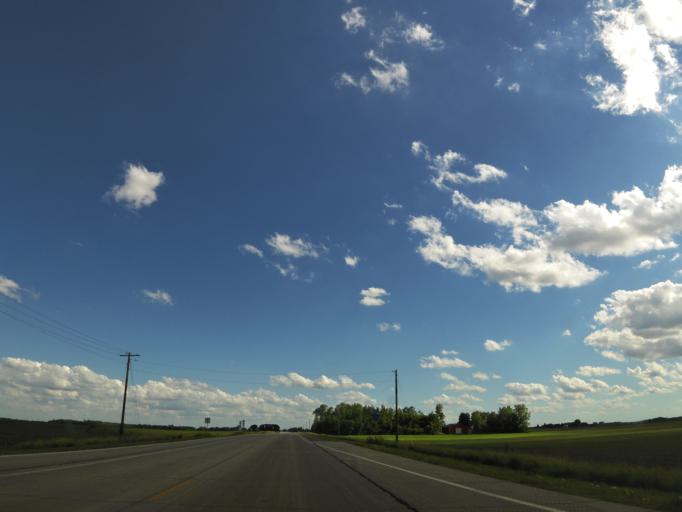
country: US
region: Minnesota
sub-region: Wright County
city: Cokato
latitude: 45.0142
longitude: -94.1755
